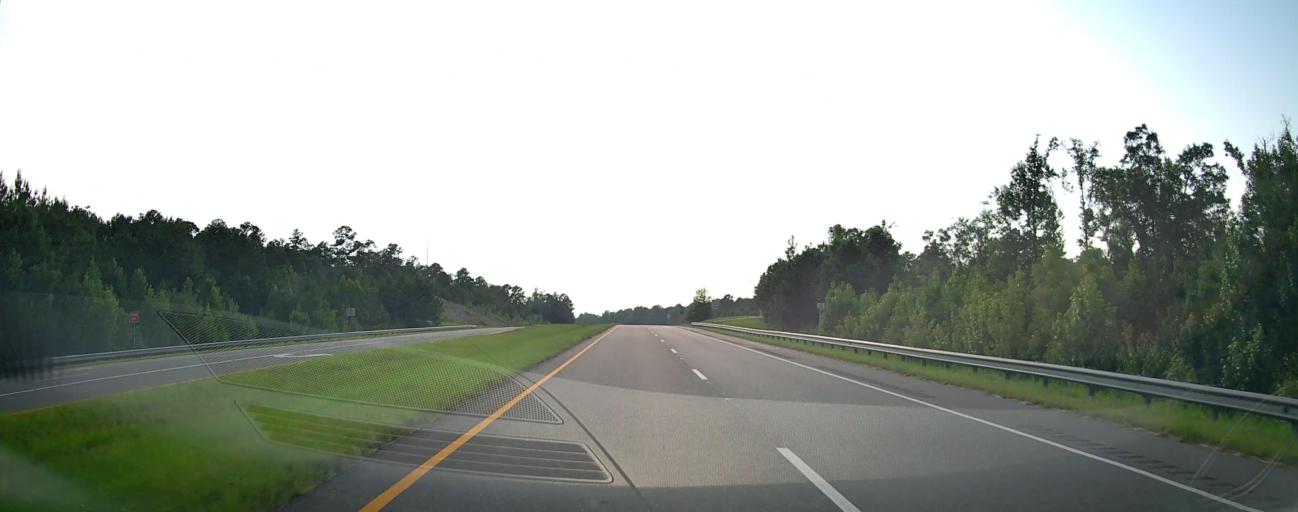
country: US
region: Georgia
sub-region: Talbot County
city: Talbotton
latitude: 32.5801
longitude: -84.5416
